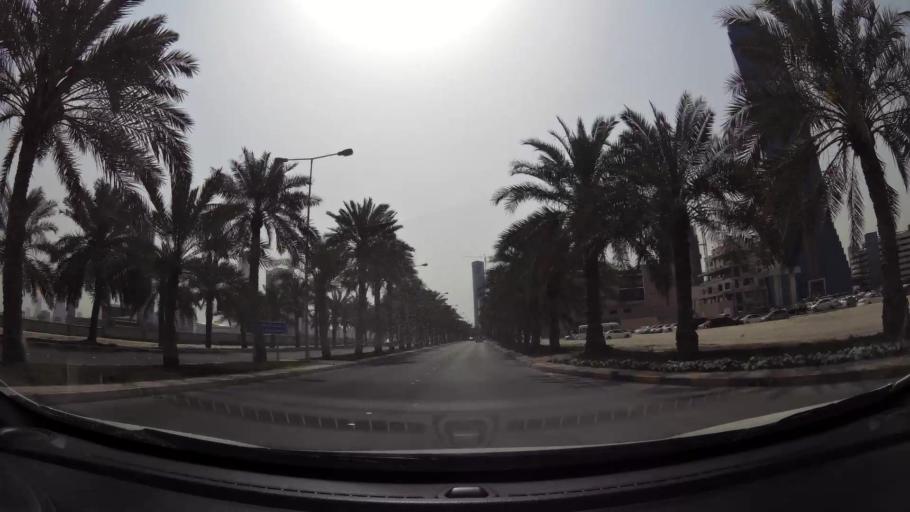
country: BH
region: Manama
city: Jidd Hafs
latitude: 26.2381
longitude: 50.5422
